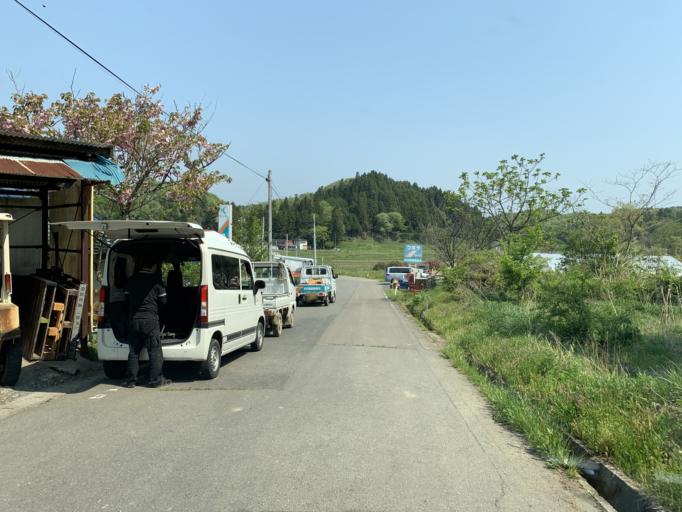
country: JP
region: Iwate
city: Ichinoseki
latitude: 38.8598
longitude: 141.0572
